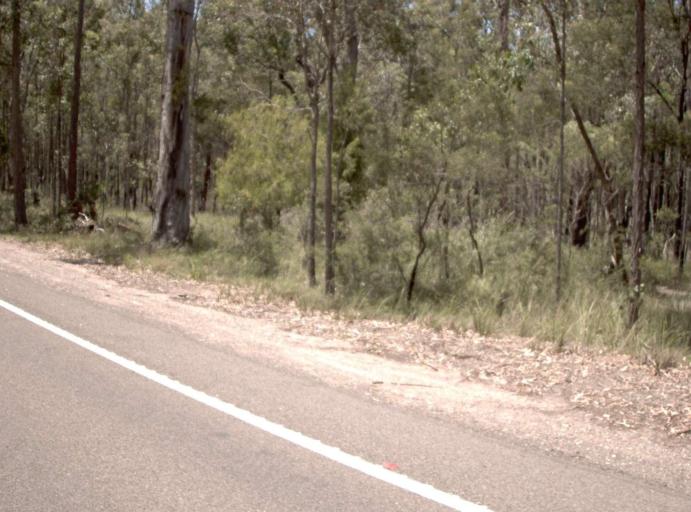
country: AU
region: Victoria
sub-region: East Gippsland
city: Lakes Entrance
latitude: -37.7726
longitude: 148.0546
